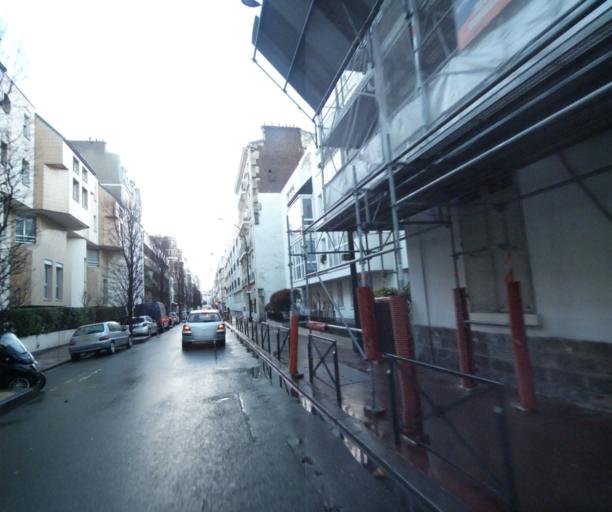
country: FR
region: Ile-de-France
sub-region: Departement des Hauts-de-Seine
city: Levallois-Perret
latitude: 48.8962
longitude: 2.2879
